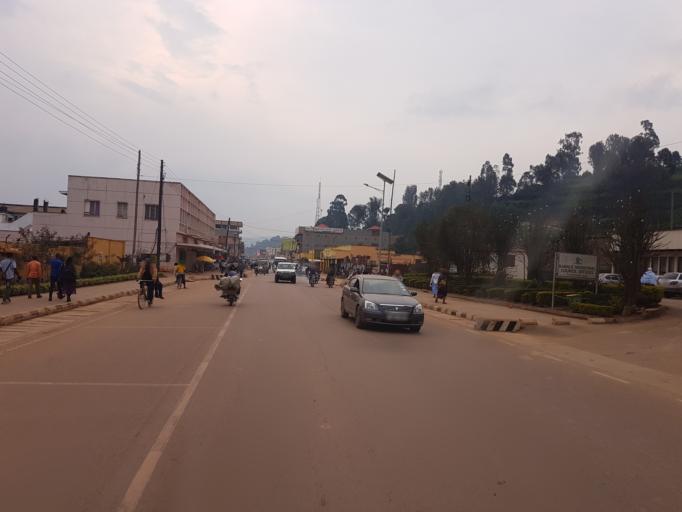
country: UG
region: Western Region
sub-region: Kabale District
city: Kabale
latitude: -1.2546
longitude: 29.9885
